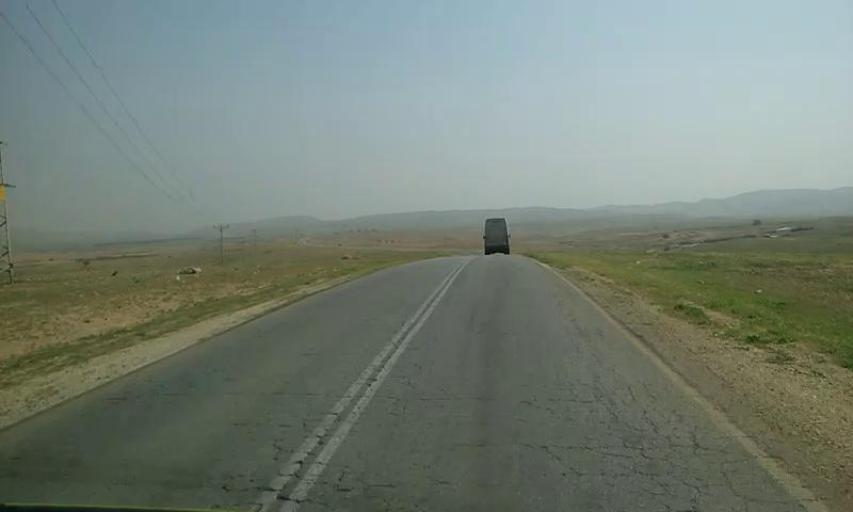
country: PS
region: West Bank
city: An Nuway`imah
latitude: 31.9200
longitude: 35.4020
